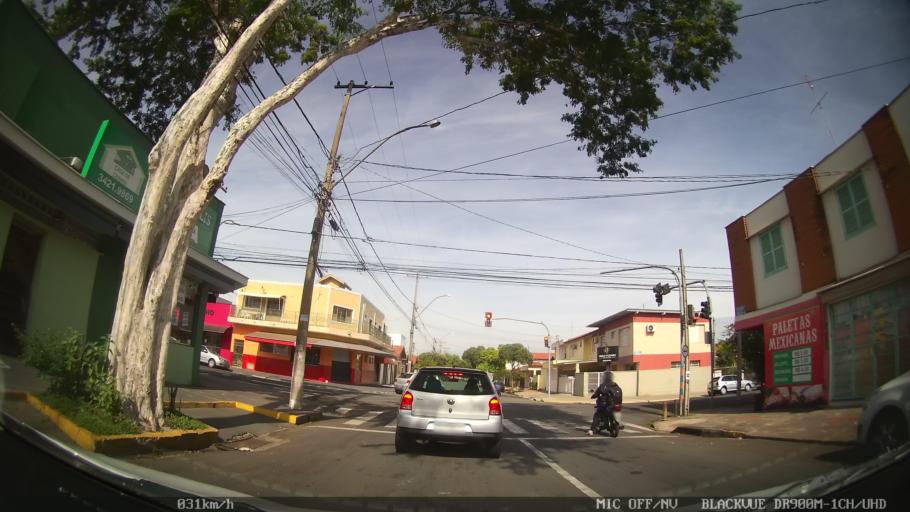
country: BR
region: Sao Paulo
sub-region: Piracicaba
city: Piracicaba
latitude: -22.7100
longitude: -47.6589
